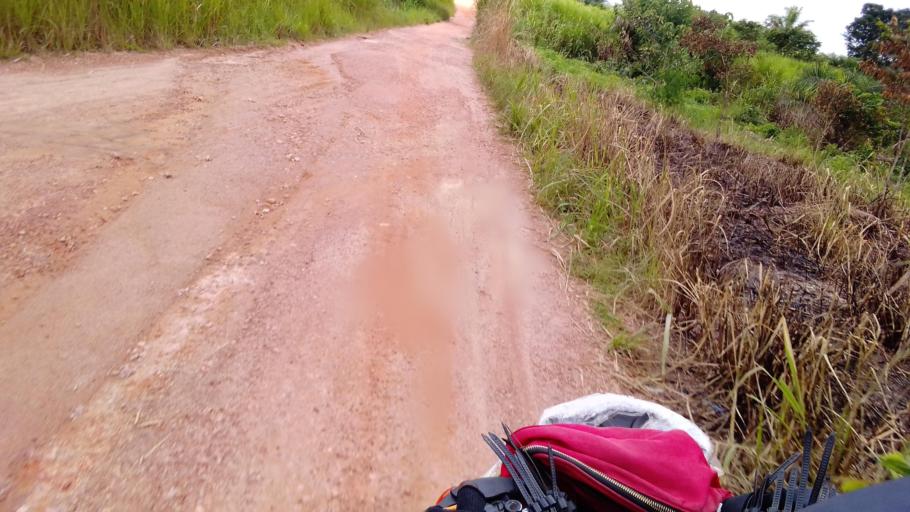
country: SL
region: Eastern Province
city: Koidu
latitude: 8.6834
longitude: -10.9573
